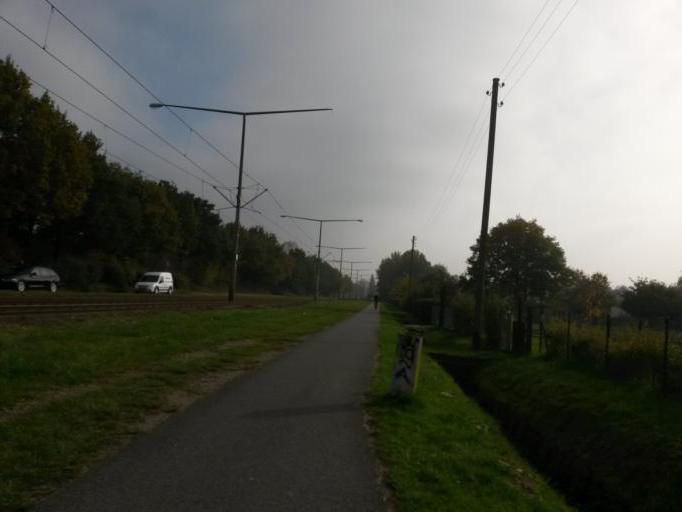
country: DE
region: Bremen
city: Bremen
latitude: 53.0774
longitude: 8.8636
